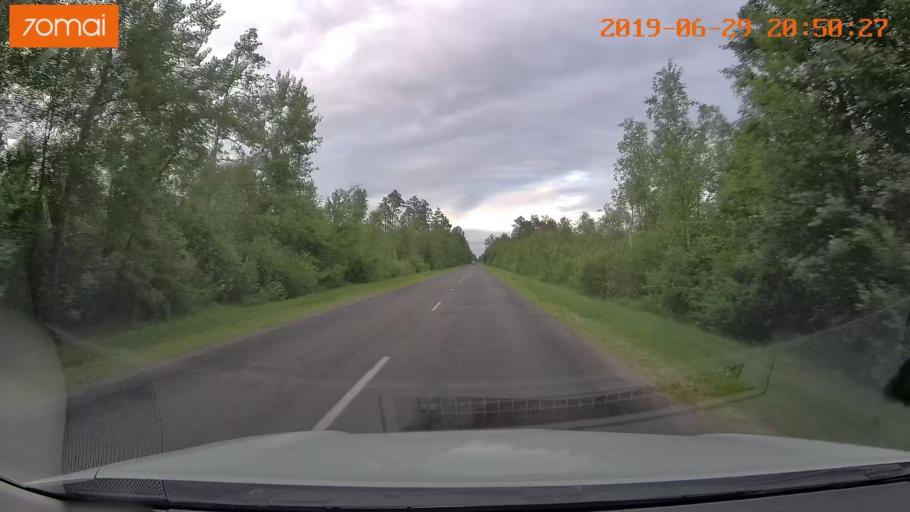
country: BY
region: Brest
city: Hantsavichy
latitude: 52.6767
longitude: 26.3361
